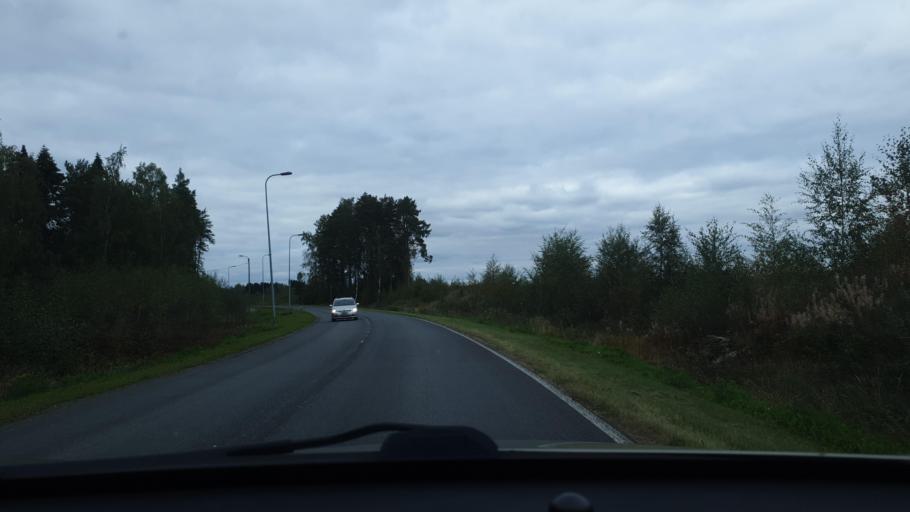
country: FI
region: Ostrobothnia
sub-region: Vaasa
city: Teeriniemi
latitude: 63.0965
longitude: 21.6986
